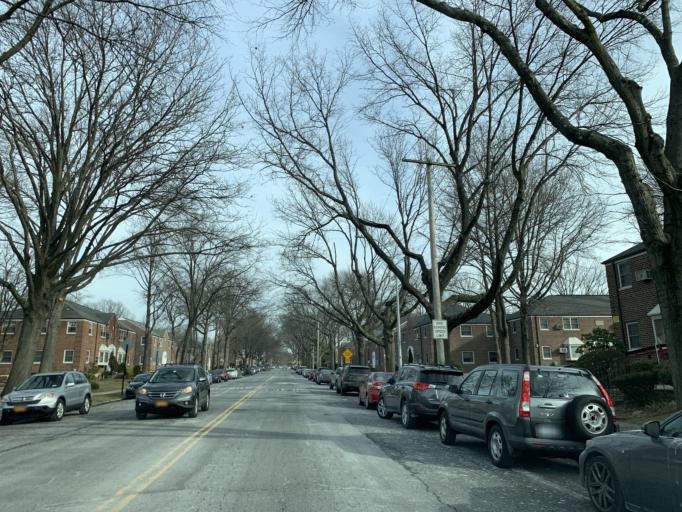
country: US
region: New York
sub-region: Nassau County
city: Lake Success
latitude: 40.7575
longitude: -73.7275
